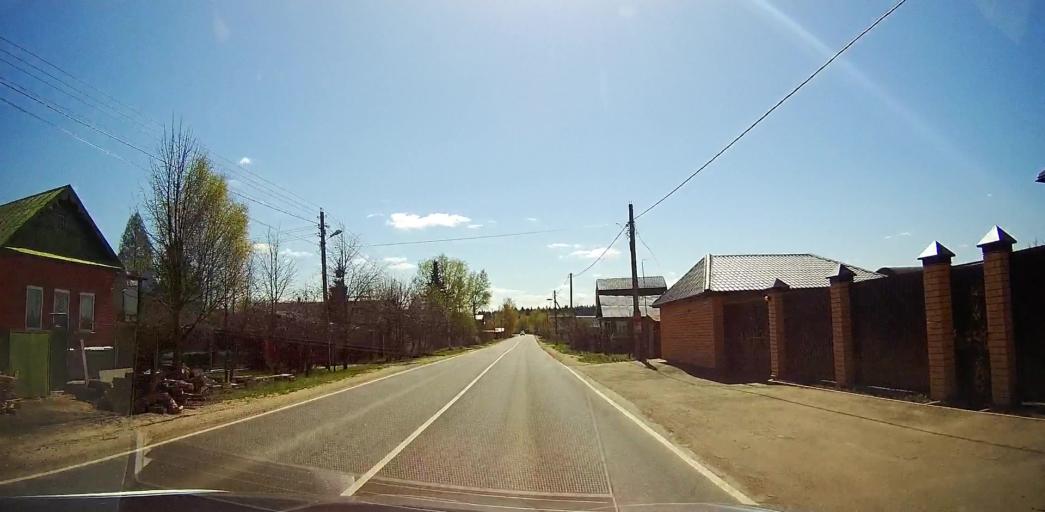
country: RU
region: Moskovskaya
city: Beloozerskiy
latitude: 55.5063
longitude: 38.4307
